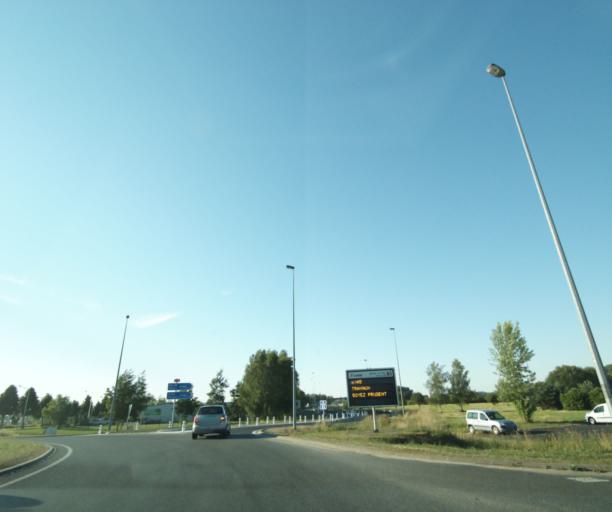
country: FR
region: Ile-de-France
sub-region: Departement de Seine-et-Marne
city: Marolles-sur-Seine
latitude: 48.3834
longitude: 3.0185
